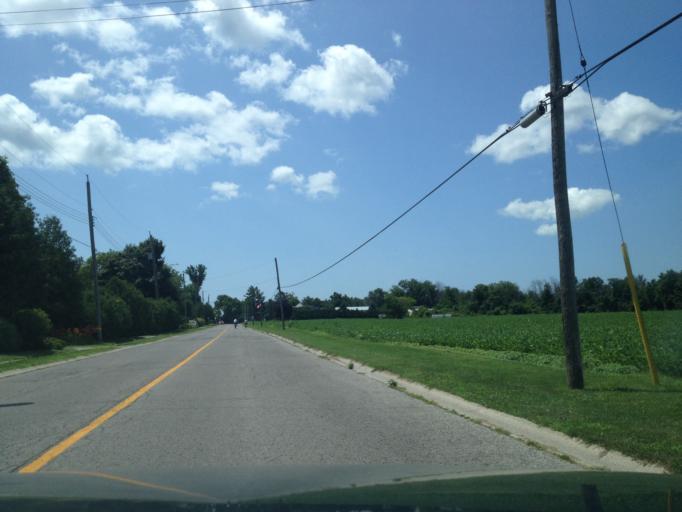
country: CA
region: Ontario
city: Norfolk County
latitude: 42.6319
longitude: -80.4430
